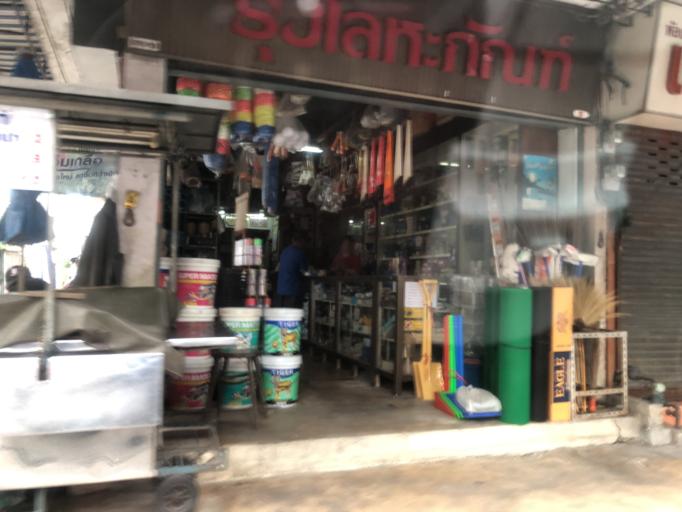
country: TH
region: Bangkok
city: Don Mueang
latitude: 13.9252
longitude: 100.5989
